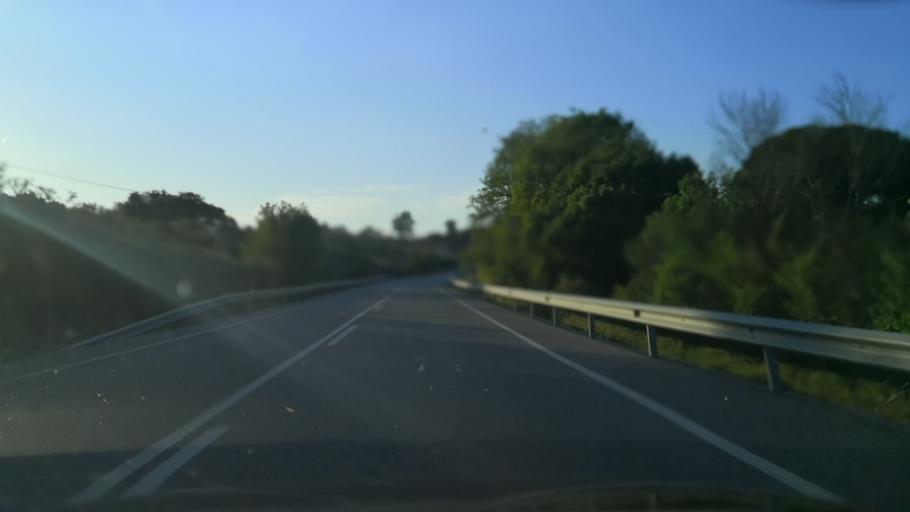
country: ES
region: Extremadura
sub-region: Provincia de Caceres
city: Valencia de Alcantara
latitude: 39.3961
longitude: -7.2480
